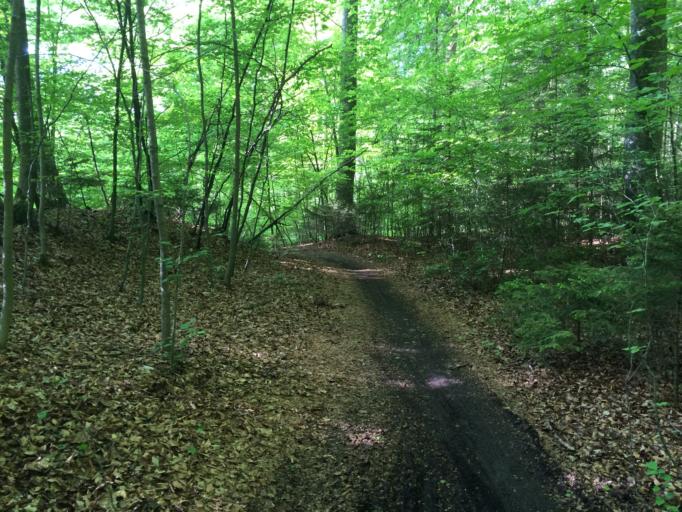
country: DE
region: Bavaria
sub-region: Upper Bavaria
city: Pullach im Isartal
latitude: 48.0537
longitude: 11.5263
